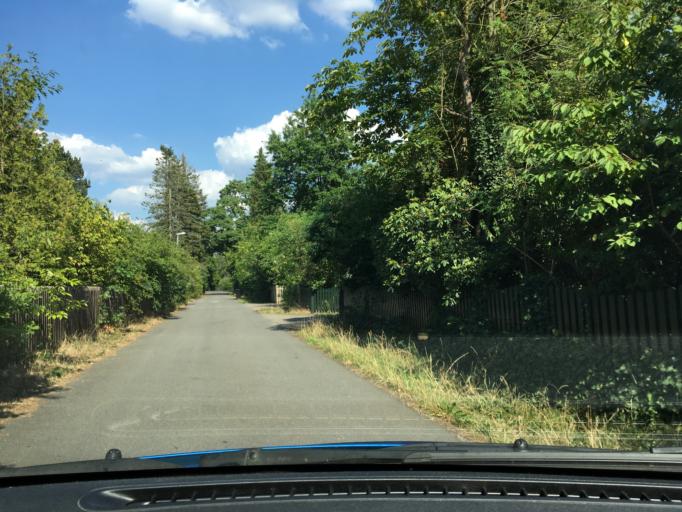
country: DE
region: Lower Saxony
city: Salzhausen
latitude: 53.2180
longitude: 10.2006
